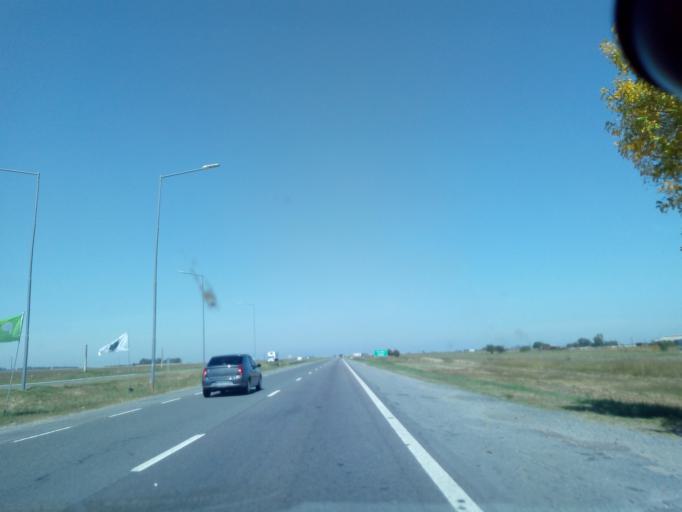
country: AR
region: Buenos Aires
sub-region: Partido de General Guido
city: General Guido
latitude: -36.6527
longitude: -57.7880
